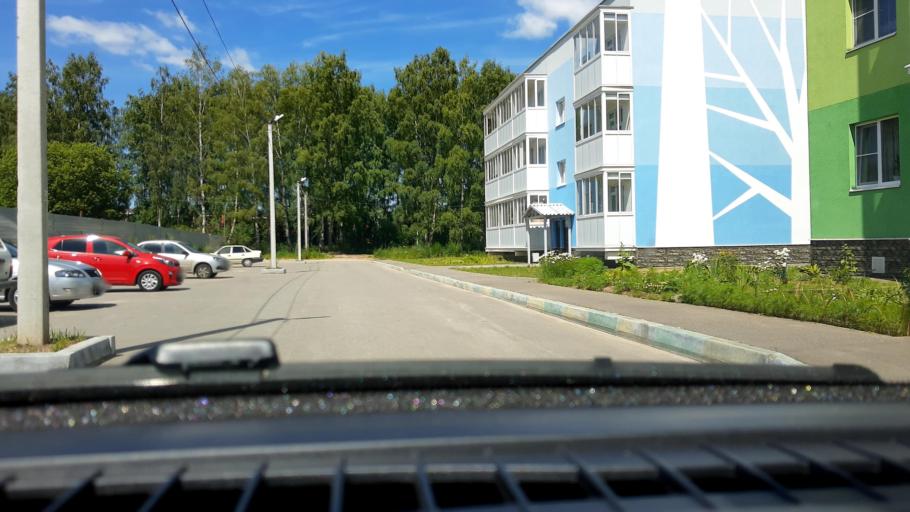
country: RU
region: Nizjnij Novgorod
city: Afonino
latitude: 56.2121
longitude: 44.0891
